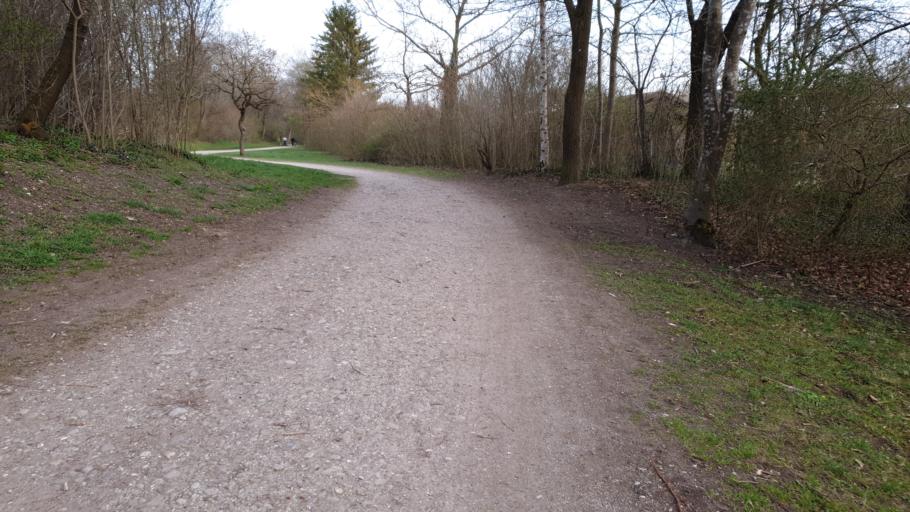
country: DE
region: Bavaria
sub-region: Upper Bavaria
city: Grobenzell
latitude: 48.1760
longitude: 11.3887
